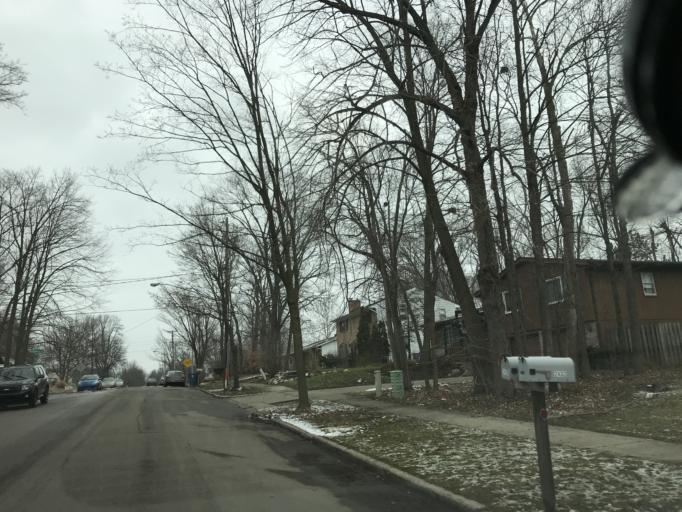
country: US
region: Michigan
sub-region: Kent County
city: East Grand Rapids
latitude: 42.9185
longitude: -85.5931
